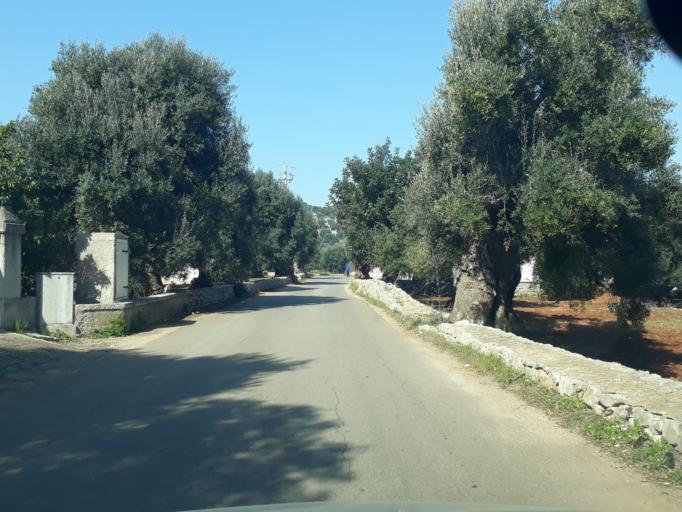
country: IT
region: Apulia
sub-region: Provincia di Brindisi
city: Fasano
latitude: 40.8374
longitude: 17.3499
